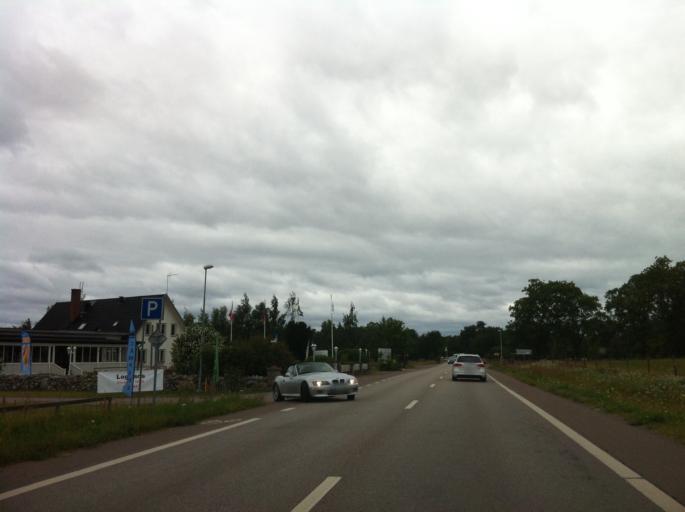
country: SE
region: Kalmar
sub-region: Borgholms Kommun
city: Borgholm
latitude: 57.2516
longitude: 17.0556
